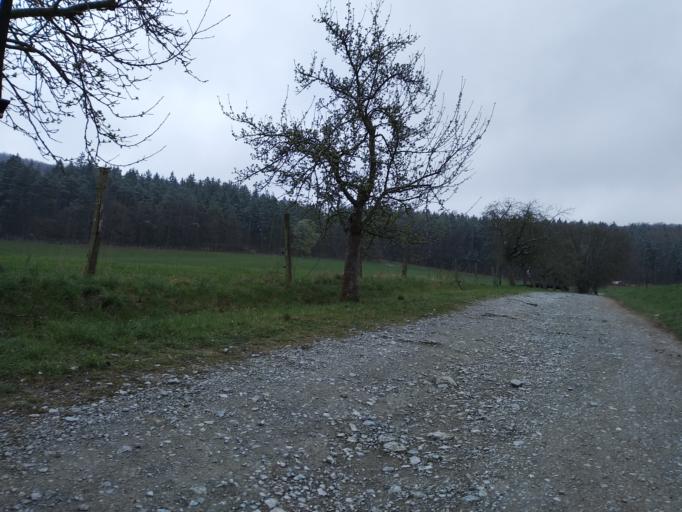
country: DE
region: Thuringia
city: Buchfart
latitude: 50.9179
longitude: 11.3327
